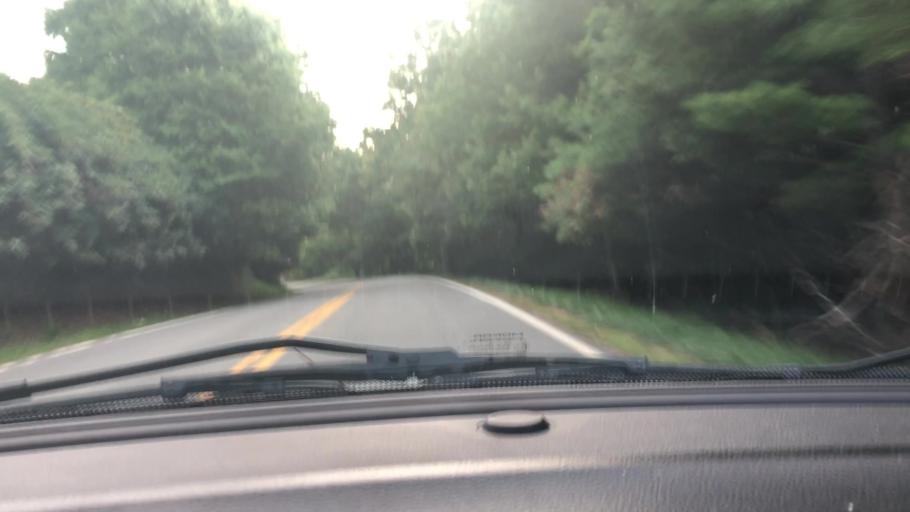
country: US
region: Virginia
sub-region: Patrick County
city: Stuart
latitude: 36.7145
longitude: -80.3361
